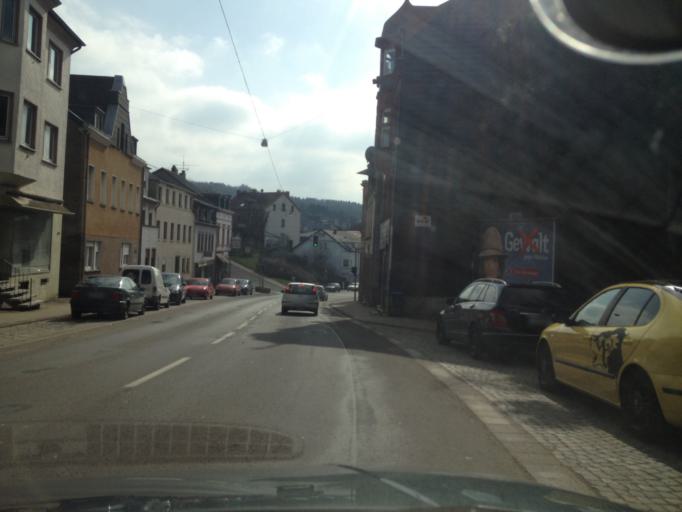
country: DE
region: Saarland
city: Friedrichsthal
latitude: 49.3242
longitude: 7.0981
